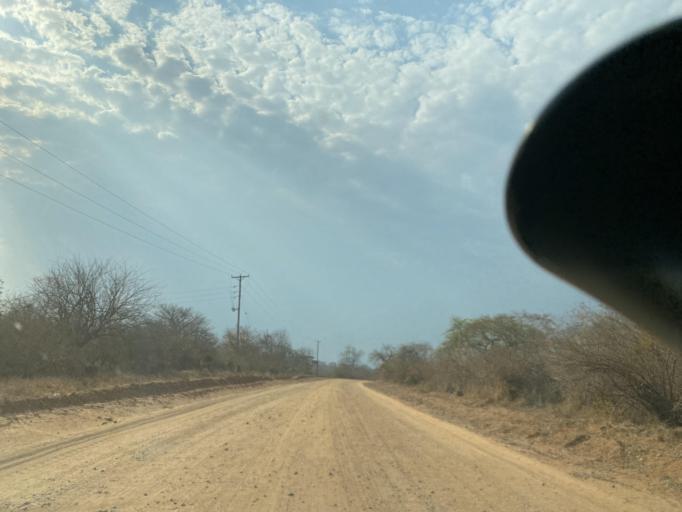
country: ZW
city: Chirundu
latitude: -15.9364
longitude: 28.9305
